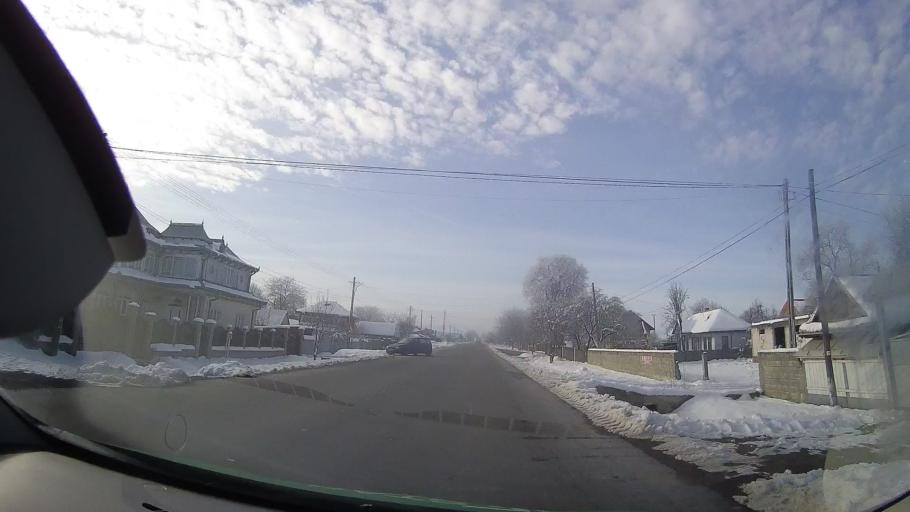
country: RO
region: Neamt
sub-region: Comuna Timisesti
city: Dumbrava
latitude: 47.2199
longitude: 26.4611
